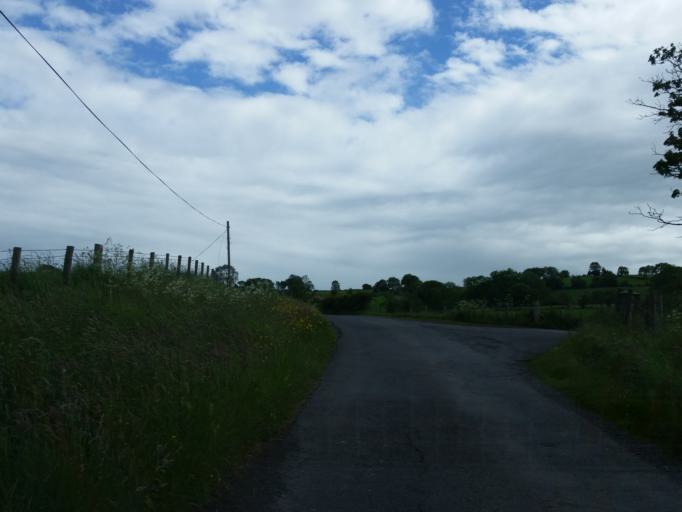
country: GB
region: Northern Ireland
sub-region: Omagh District
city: Omagh
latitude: 54.5476
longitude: -7.1331
